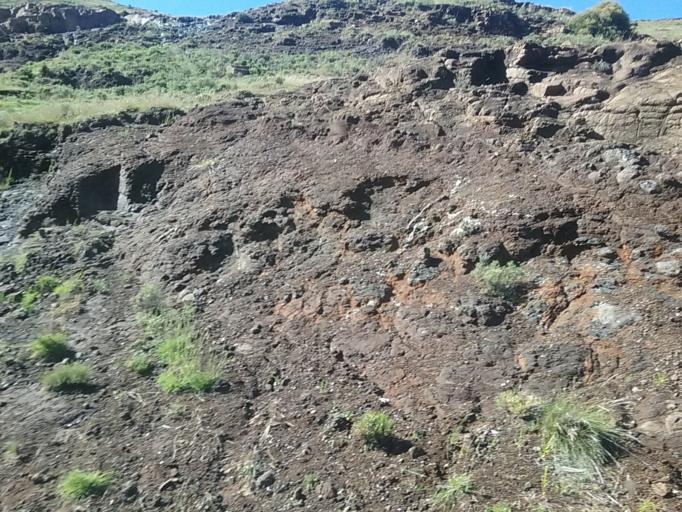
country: LS
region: Berea
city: Teyateyaneng
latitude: -29.2320
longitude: 27.9249
